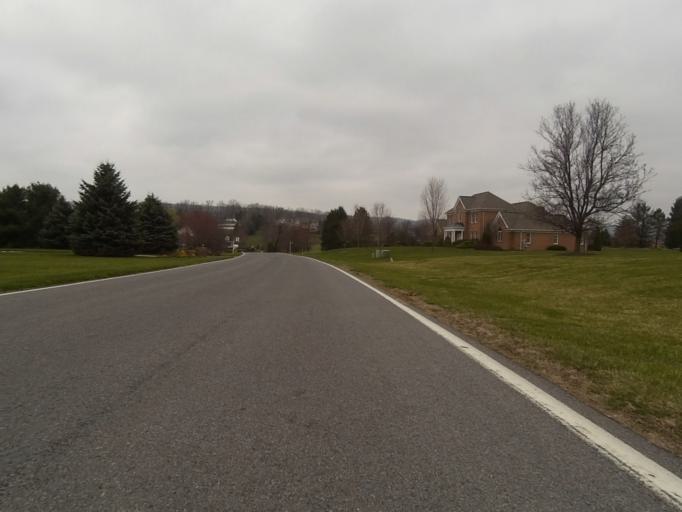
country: US
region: Pennsylvania
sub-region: Centre County
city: Boalsburg
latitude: 40.7891
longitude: -77.7601
